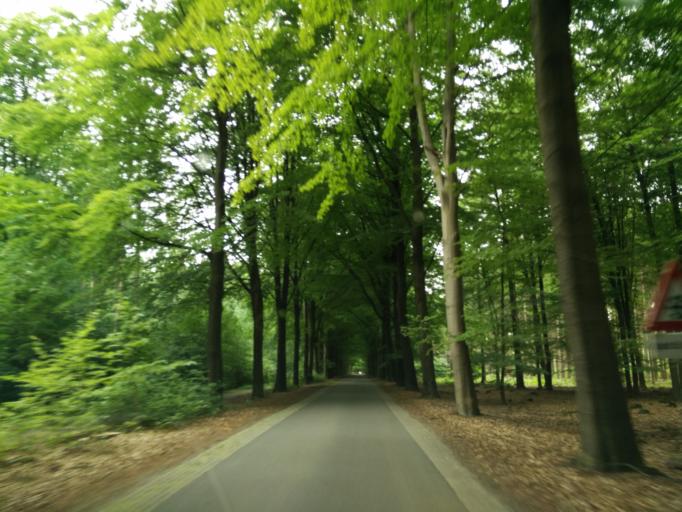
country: NL
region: Drenthe
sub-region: Gemeente Borger-Odoorn
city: Borger
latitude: 52.9502
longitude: 6.7516
